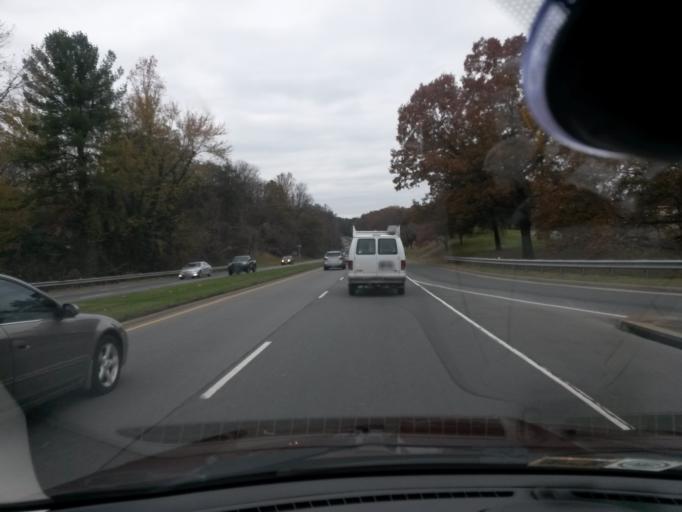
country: US
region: Virginia
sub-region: City of Charlottesville
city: Charlottesville
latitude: 38.0469
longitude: -78.4793
